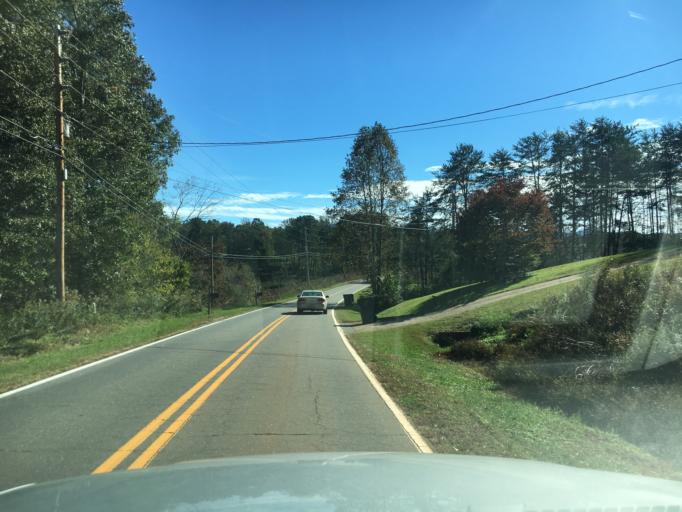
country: US
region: North Carolina
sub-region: Burke County
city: Salem
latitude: 35.7093
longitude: -81.7354
